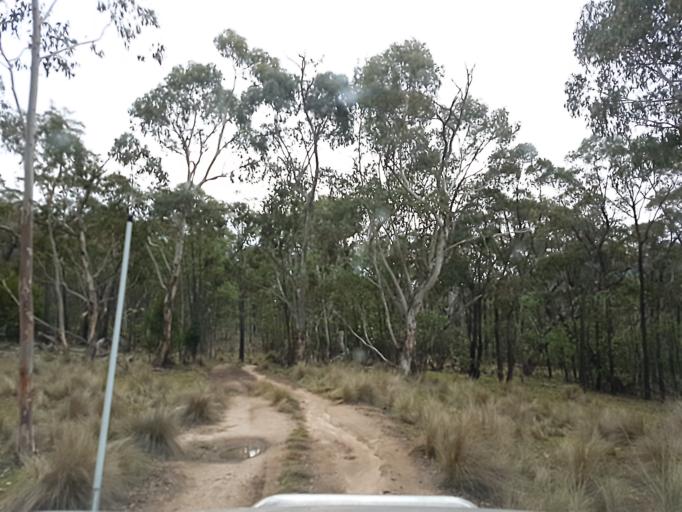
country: AU
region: New South Wales
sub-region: Snowy River
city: Jindabyne
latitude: -36.8828
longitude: 148.3381
